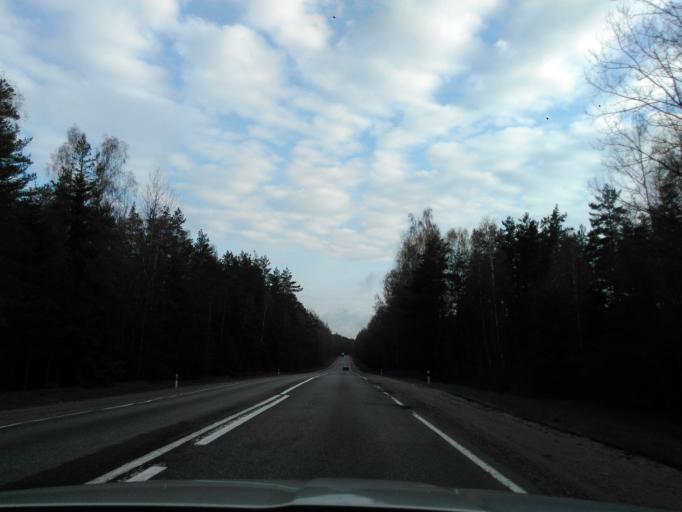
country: BY
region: Minsk
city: Lahoysk
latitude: 54.3166
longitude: 27.8755
